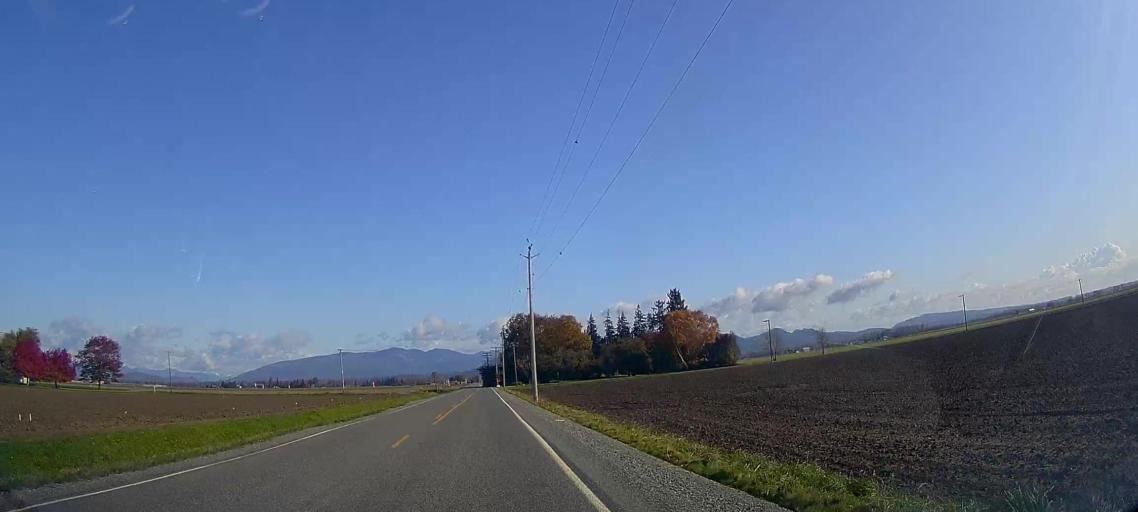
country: US
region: Washington
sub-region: Skagit County
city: Mount Vernon
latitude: 48.3990
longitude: -122.4244
